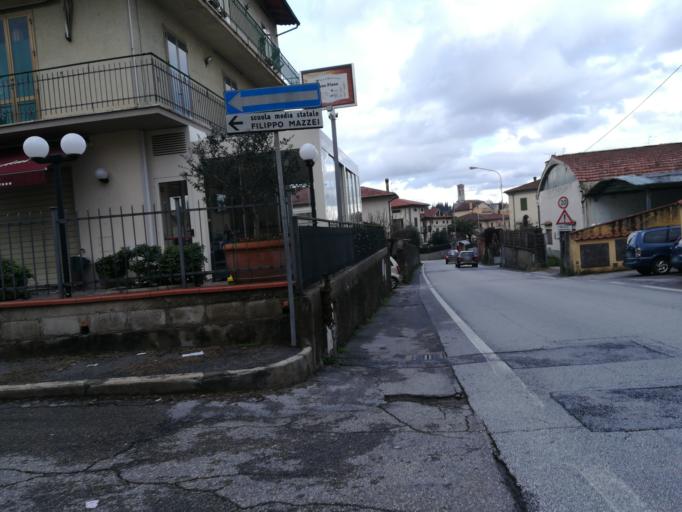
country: IT
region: Tuscany
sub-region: Provincia di Prato
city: Poggio A Caiano
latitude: 43.8112
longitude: 11.0526
